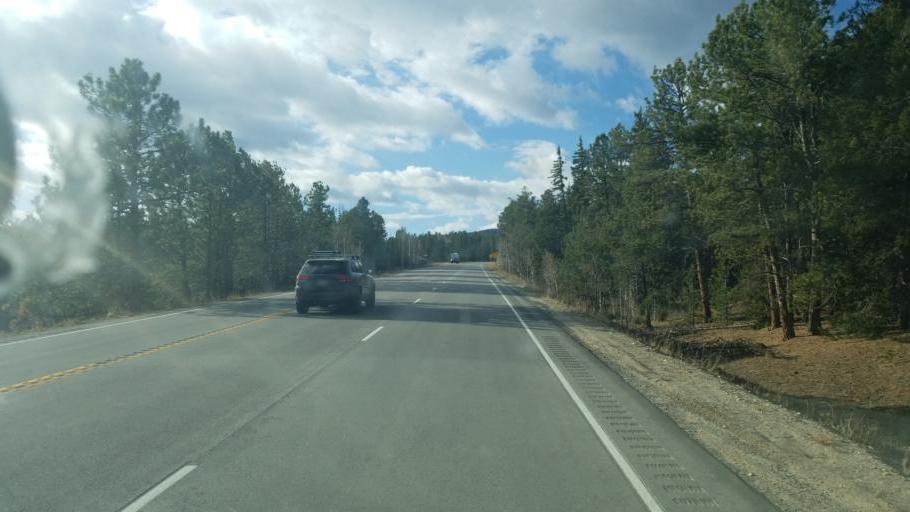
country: US
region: Colorado
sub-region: Chaffee County
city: Buena Vista
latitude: 38.9173
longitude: -105.9692
